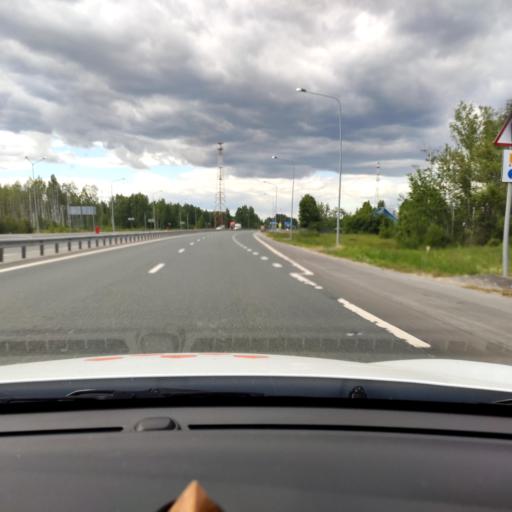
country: RU
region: Mariy-El
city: Surok
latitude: 56.4378
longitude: 48.1160
